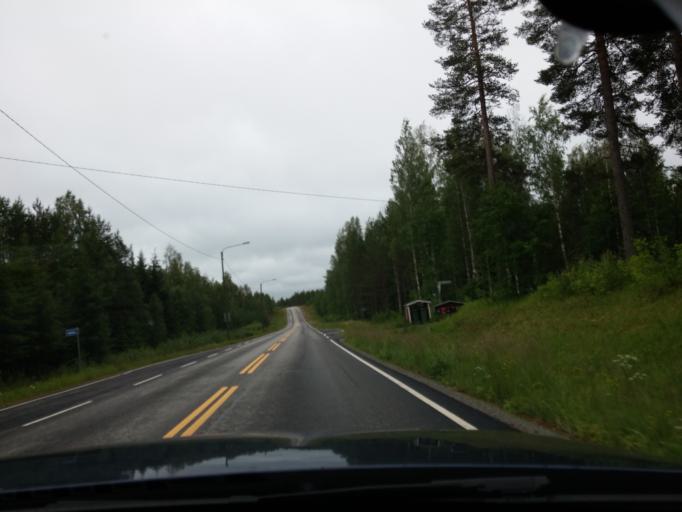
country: FI
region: Central Finland
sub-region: Saarijaervi-Viitasaari
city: Pylkoenmaeki
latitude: 62.6412
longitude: 24.8431
